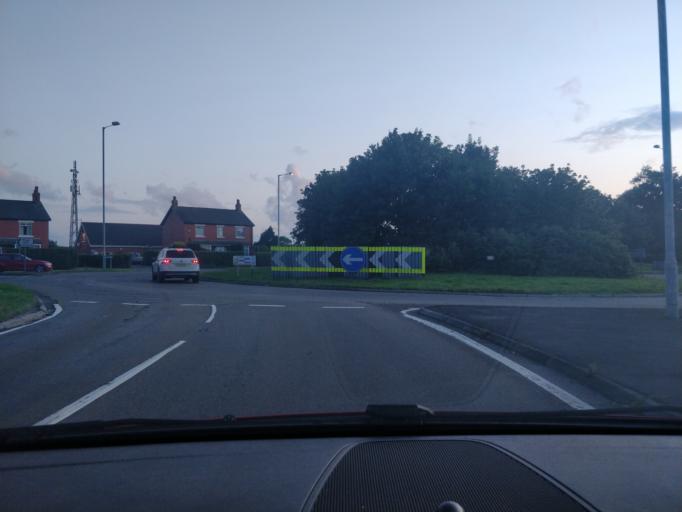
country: GB
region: England
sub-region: Lancashire
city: Croston
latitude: 53.7130
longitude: -2.7779
